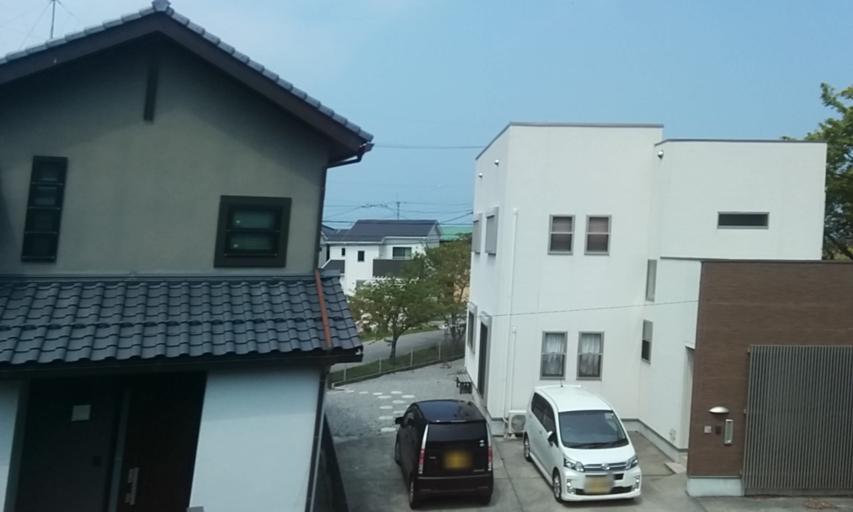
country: JP
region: Shiga Prefecture
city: Hikone
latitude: 35.2832
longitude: 136.2644
